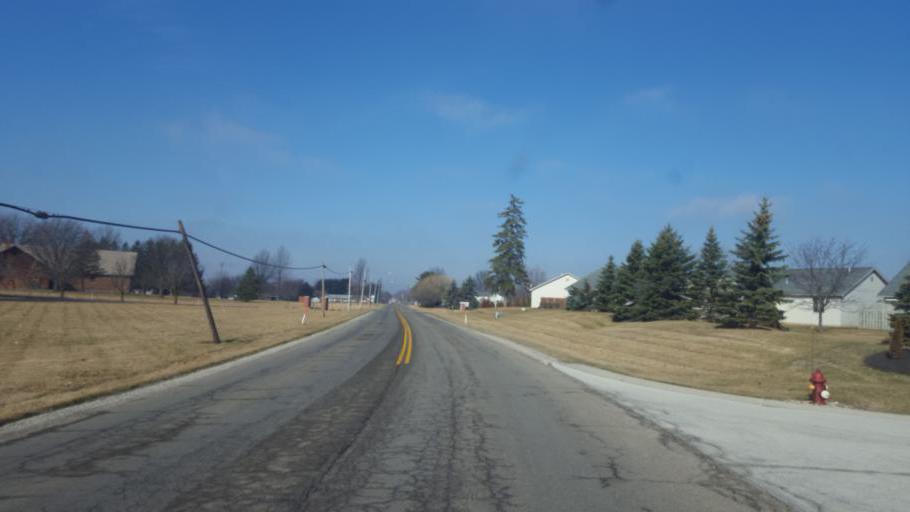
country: US
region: Ohio
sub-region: Crawford County
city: Bucyrus
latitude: 40.7931
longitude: -82.9511
